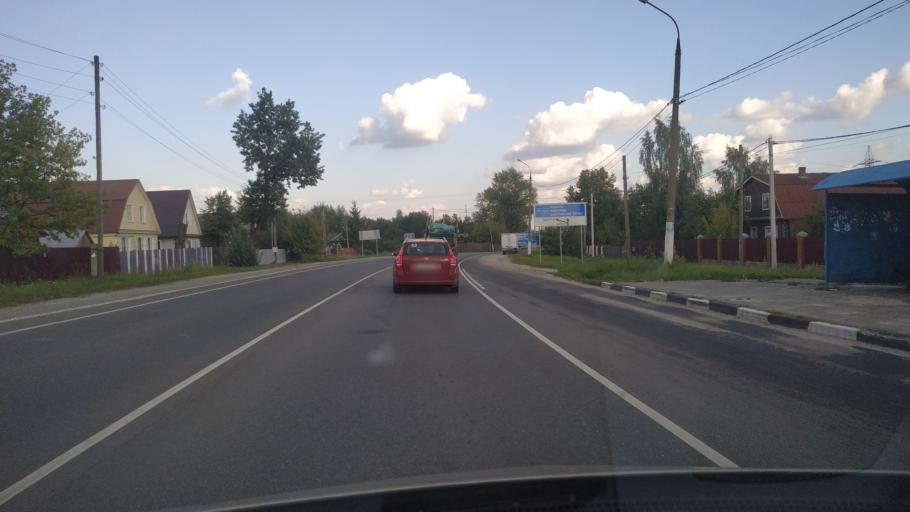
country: RU
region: Moskovskaya
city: Shatura
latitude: 55.5768
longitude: 39.4964
